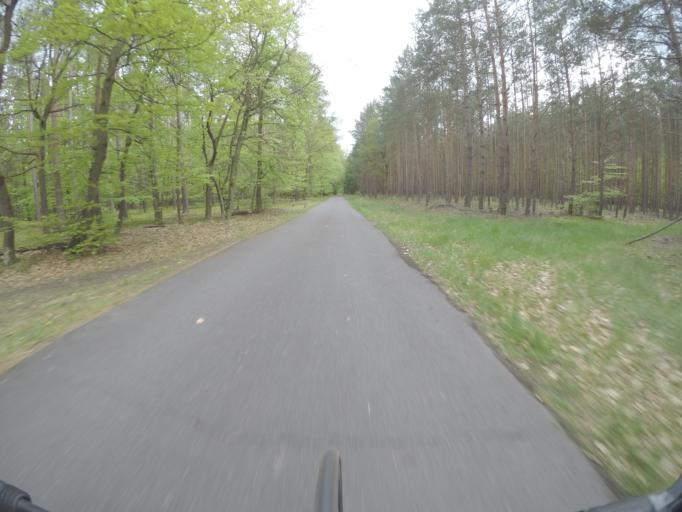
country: DE
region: Brandenburg
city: Biesenthal
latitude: 52.8082
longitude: 13.6319
